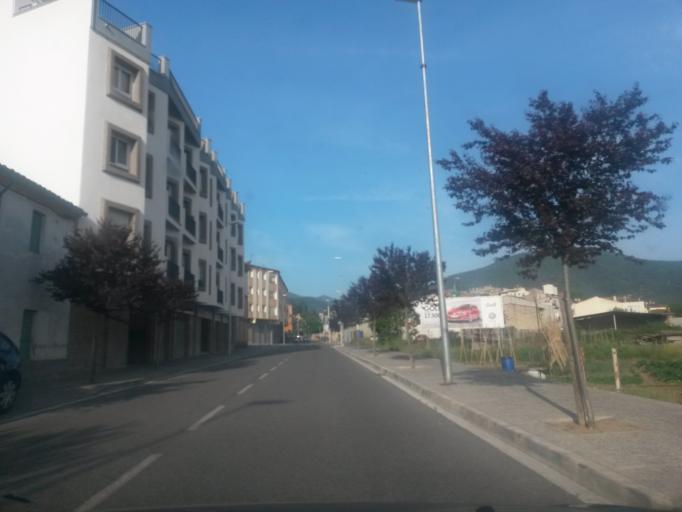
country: ES
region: Catalonia
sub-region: Provincia de Girona
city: Angles
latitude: 41.9575
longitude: 2.6450
